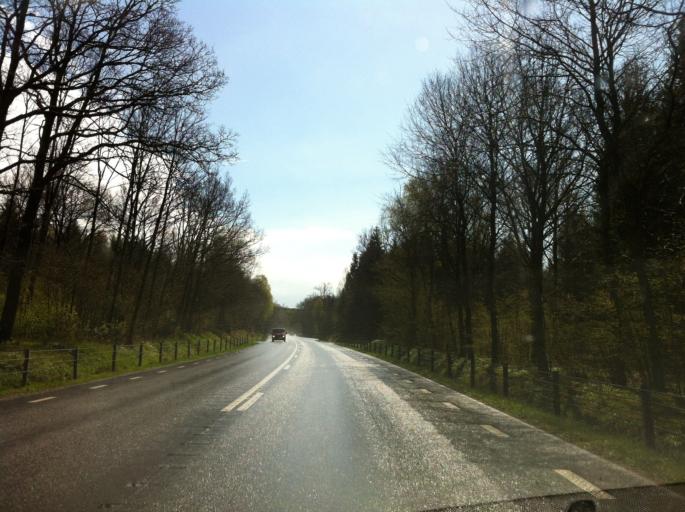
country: SE
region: Skane
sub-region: Hoors Kommun
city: Satofta
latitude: 55.9006
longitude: 13.6141
